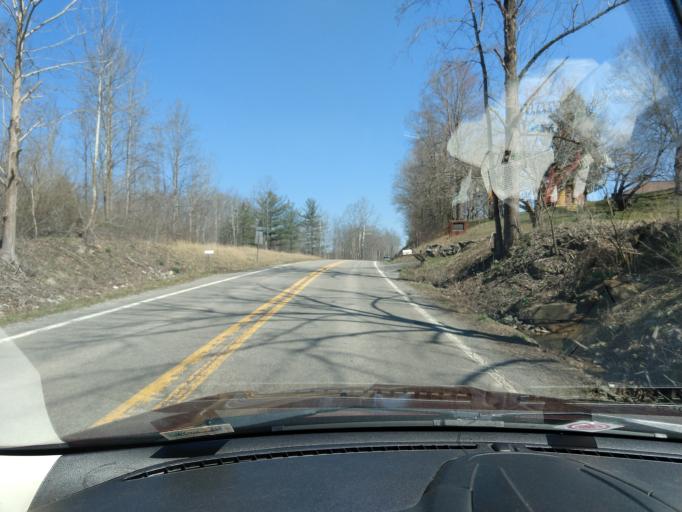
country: US
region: West Virginia
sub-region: Braxton County
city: Sutton
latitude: 38.6927
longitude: -80.6721
